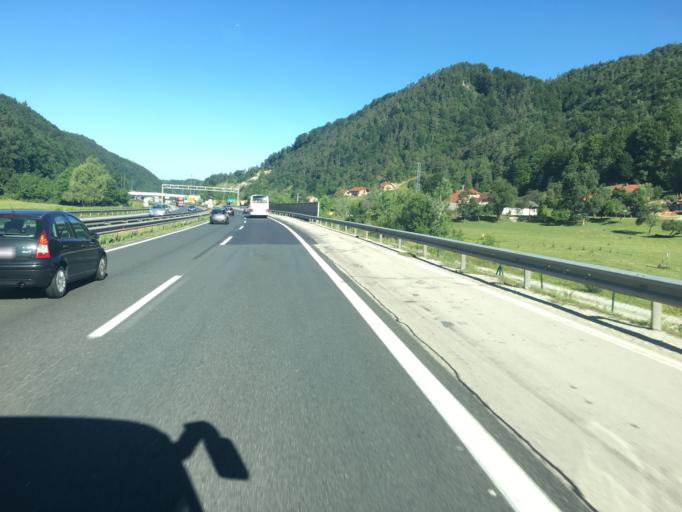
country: SI
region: Moravce
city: Moravce
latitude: 46.1703
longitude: 14.7323
